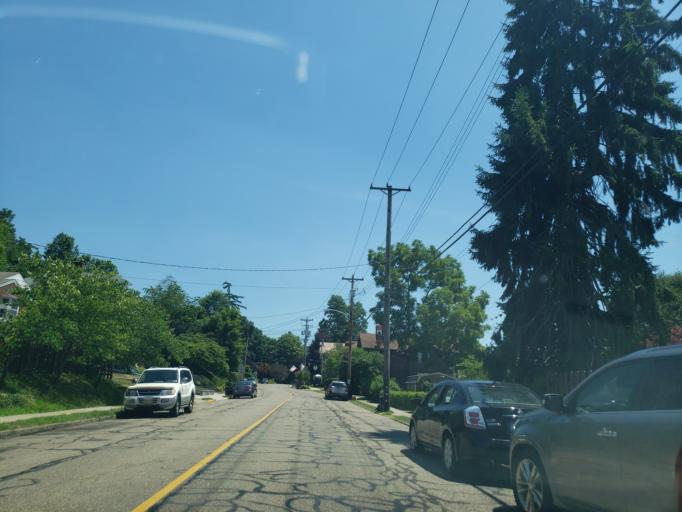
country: US
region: Pennsylvania
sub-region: Allegheny County
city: Emsworth
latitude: 40.5132
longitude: -80.0968
